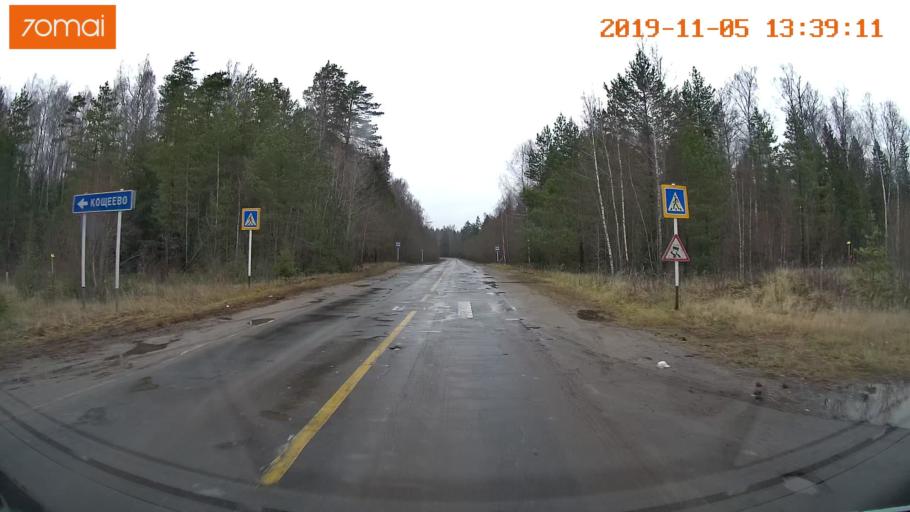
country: RU
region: Ivanovo
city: Shuya
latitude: 56.9377
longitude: 41.3869
